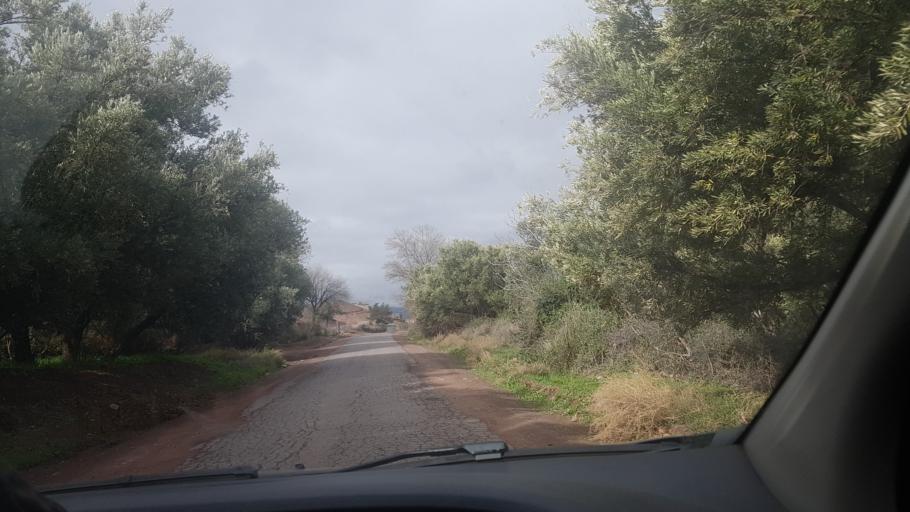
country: MA
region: Marrakech-Tensift-Al Haouz
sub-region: Al-Haouz
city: Azgour
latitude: 30.9992
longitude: -8.1625
